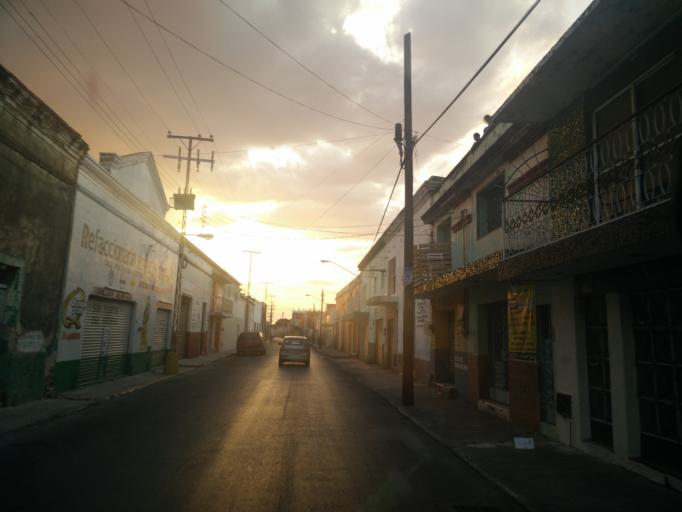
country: MX
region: Yucatan
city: Merida
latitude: 20.9622
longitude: -89.6103
